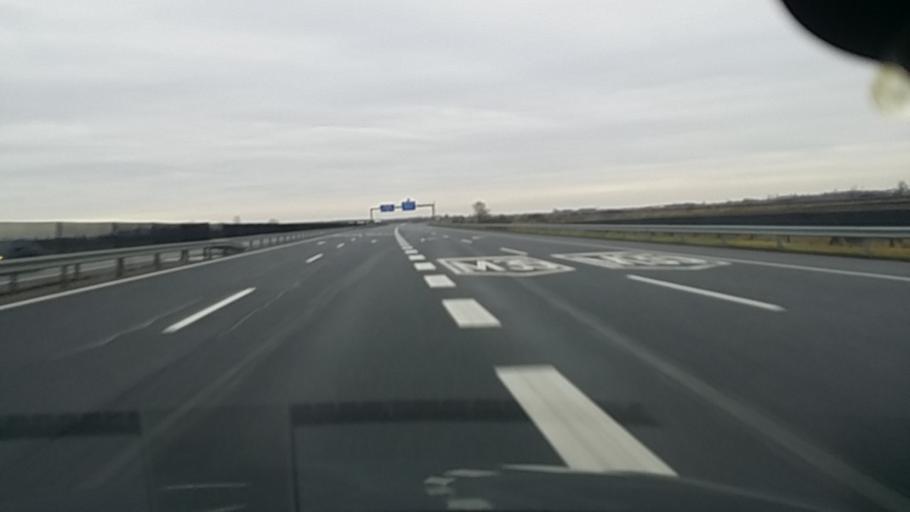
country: HU
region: Hajdu-Bihar
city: Gorbehaza
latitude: 47.7963
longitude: 21.2389
